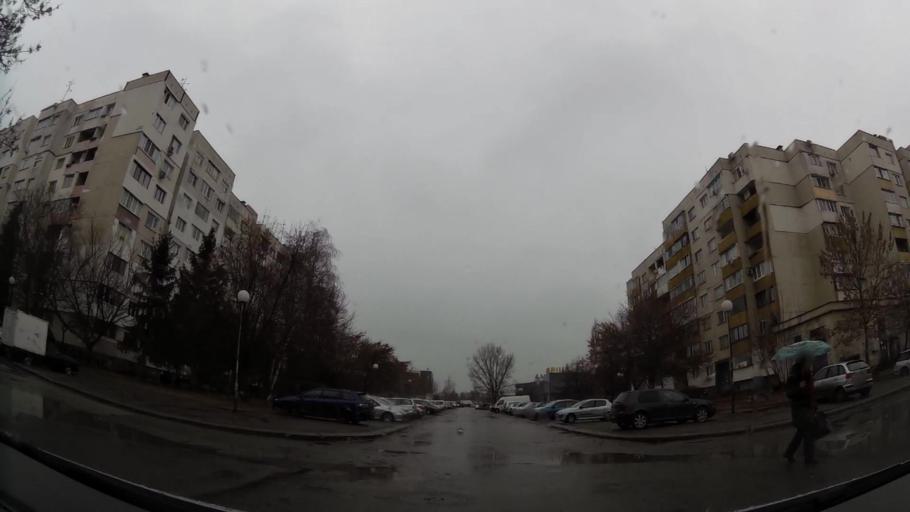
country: BG
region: Sofia-Capital
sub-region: Stolichna Obshtina
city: Sofia
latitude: 42.6434
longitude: 23.4093
